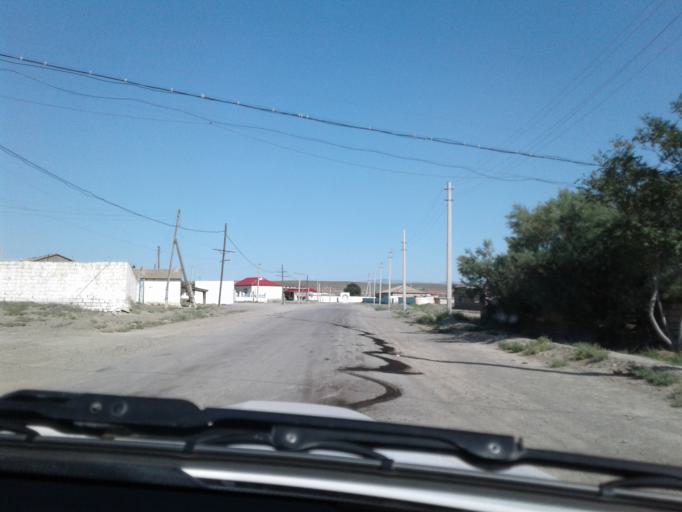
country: TM
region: Balkan
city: Serdar
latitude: 38.7128
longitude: 56.3378
